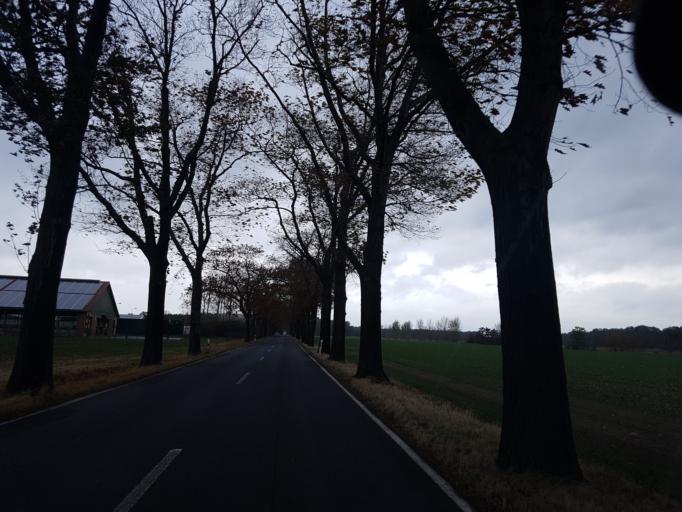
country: DE
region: Brandenburg
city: Herzberg
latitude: 51.6555
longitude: 13.2343
